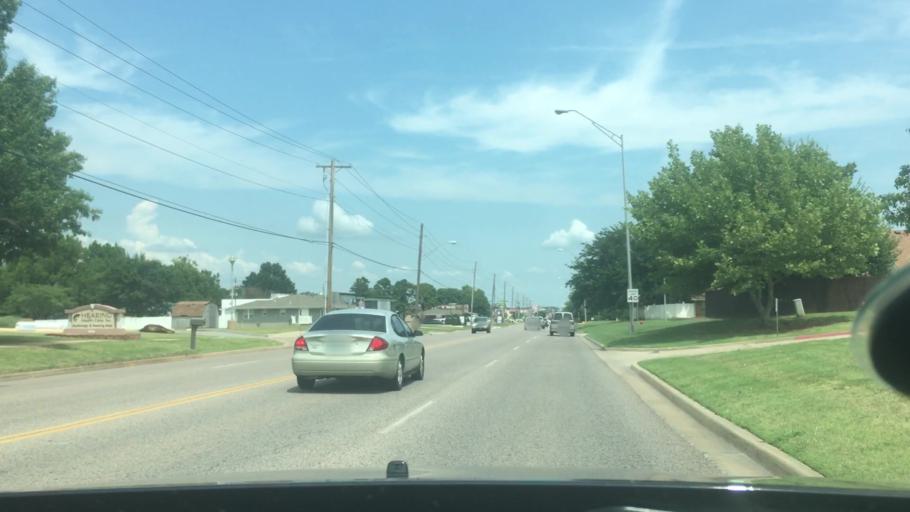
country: US
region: Oklahoma
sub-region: Pottawatomie County
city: Shawnee
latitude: 35.3715
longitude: -96.9297
